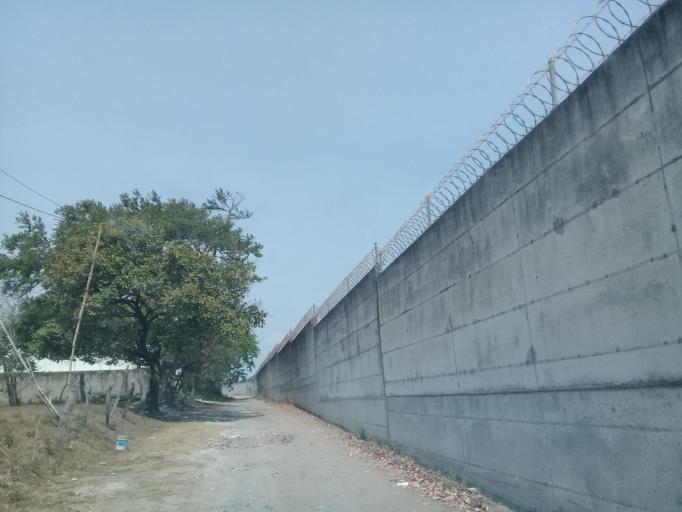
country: MX
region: Veracruz
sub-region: Veracruz
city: Hacienda Sotavento
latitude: 19.1344
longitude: -96.1805
